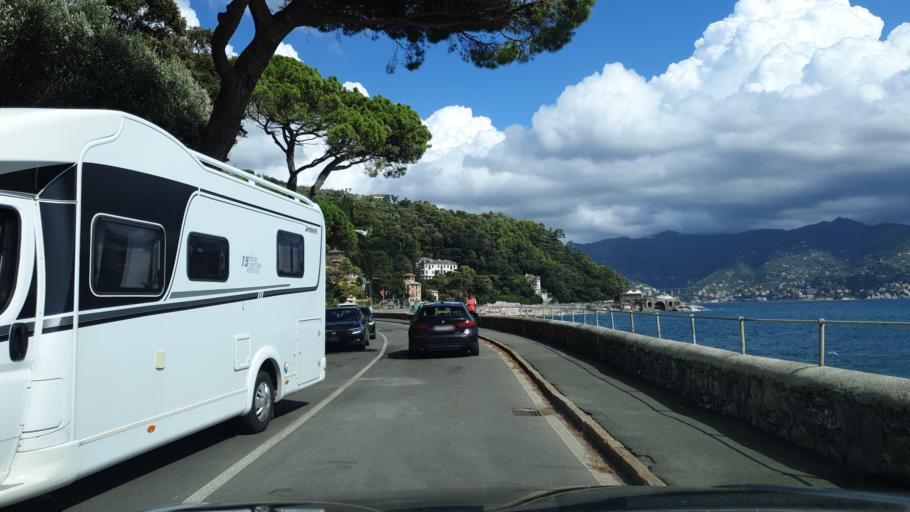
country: IT
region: Liguria
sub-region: Provincia di Genova
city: Portofino
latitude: 44.3168
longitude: 9.2116
